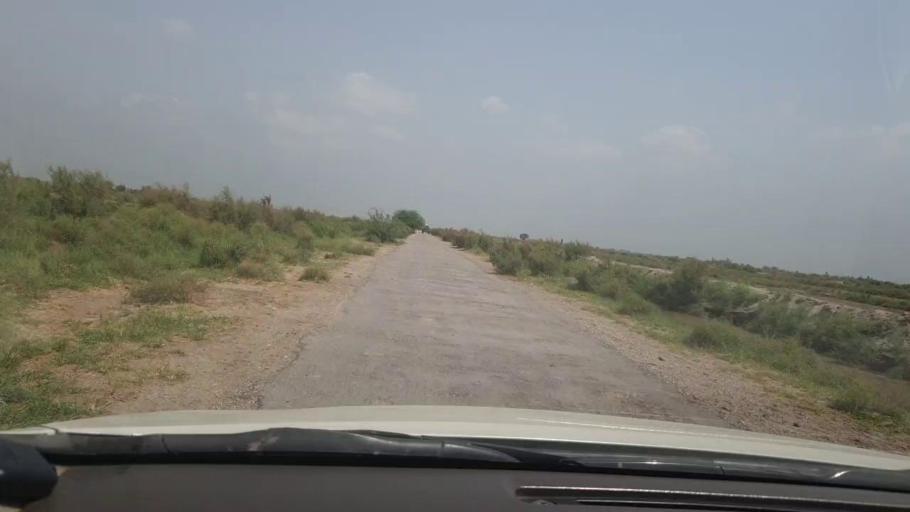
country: PK
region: Sindh
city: Garhi Yasin
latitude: 28.0126
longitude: 68.4995
